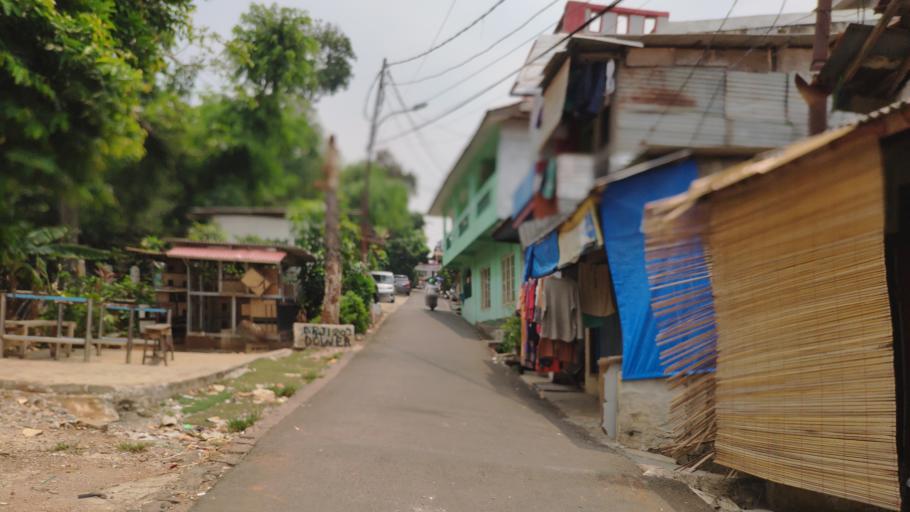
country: ID
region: Banten
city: South Tangerang
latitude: -6.2598
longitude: 106.7729
